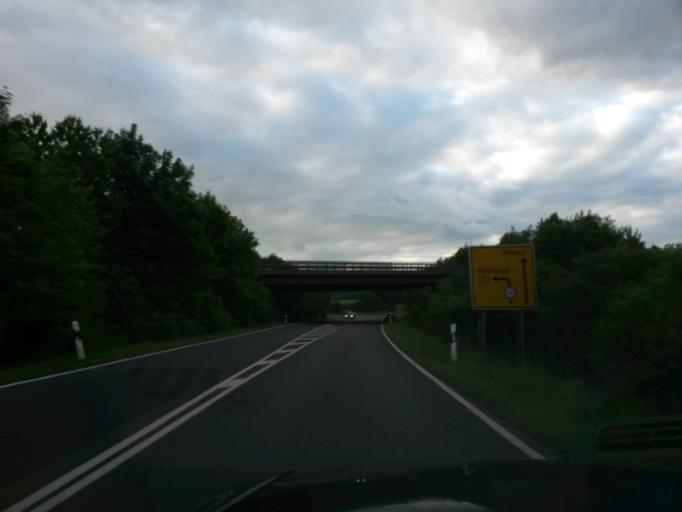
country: DE
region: Bavaria
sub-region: Regierungsbezirk Unterfranken
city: Estenfeld
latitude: 49.8259
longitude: 9.9901
